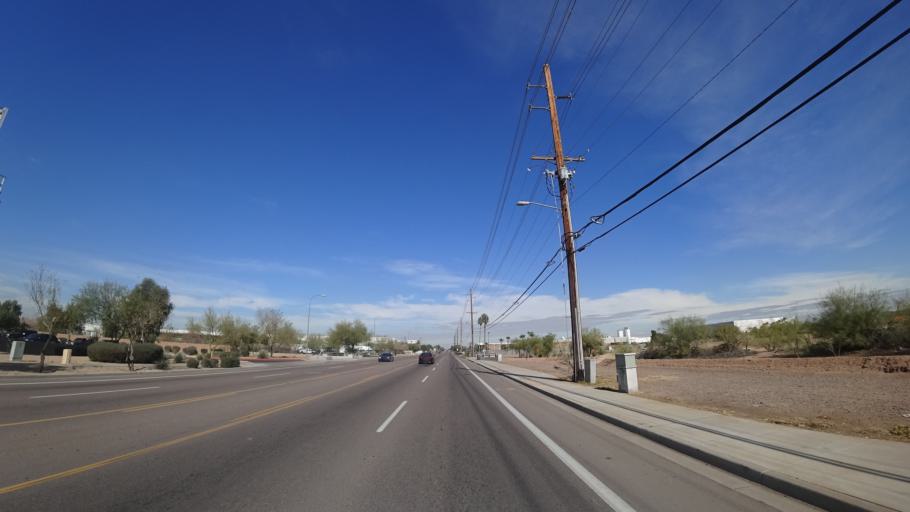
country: US
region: Arizona
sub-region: Maricopa County
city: Tolleson
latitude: 33.4402
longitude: -112.2036
